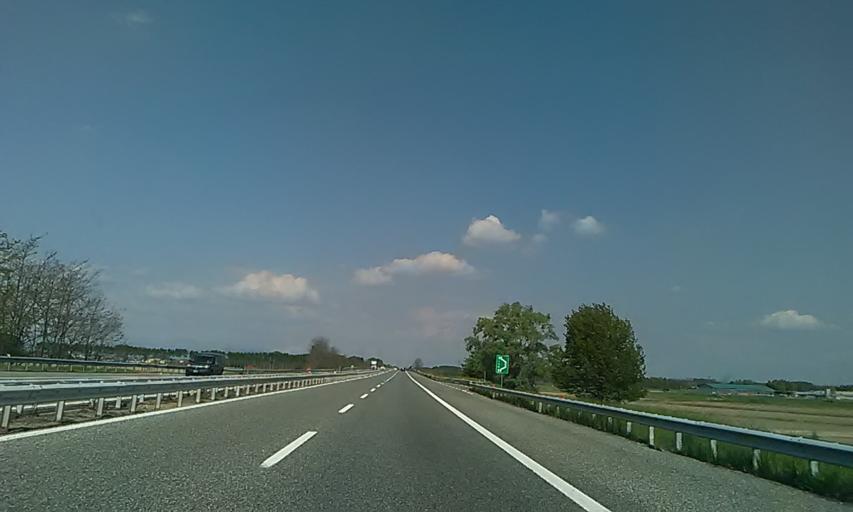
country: IT
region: Piedmont
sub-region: Provincia di Novara
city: Sillavengo
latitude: 45.5146
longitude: 8.4325
